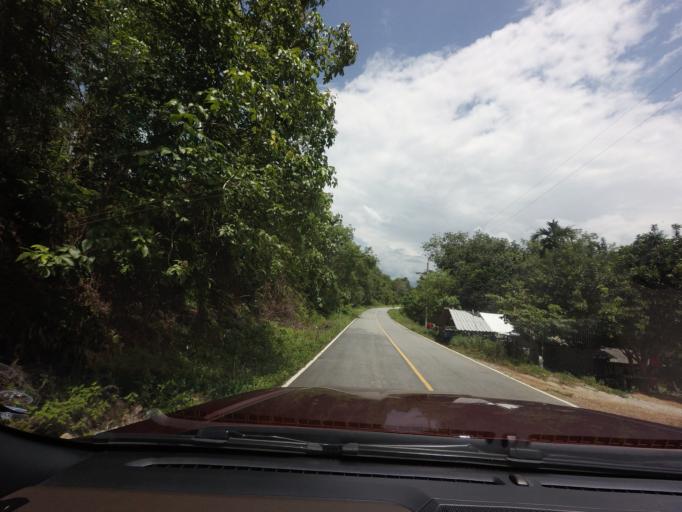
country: TH
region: Narathiwat
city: Chanae
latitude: 6.0765
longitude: 101.6878
